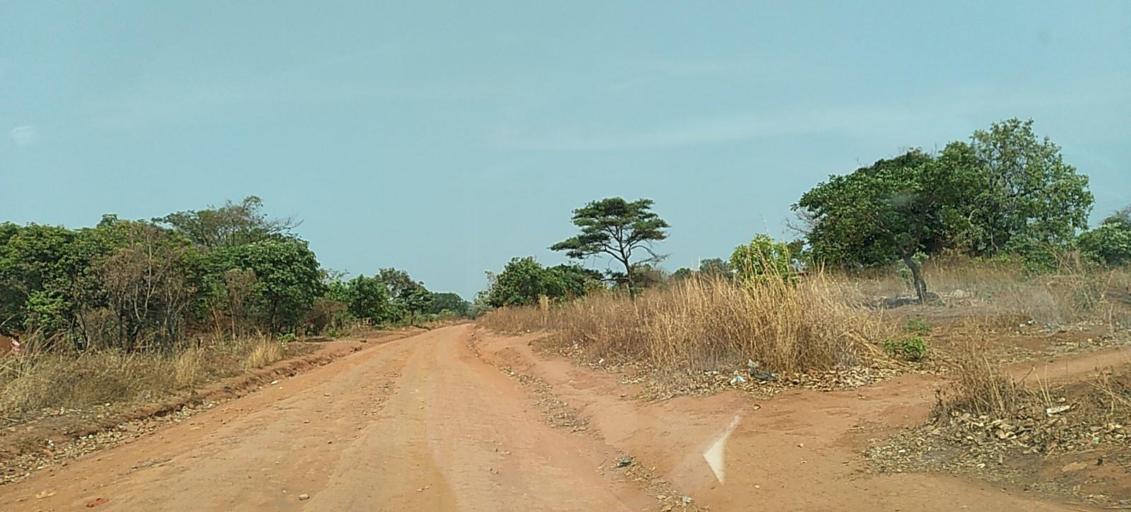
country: ZM
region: Copperbelt
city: Chililabombwe
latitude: -12.3416
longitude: 27.7103
